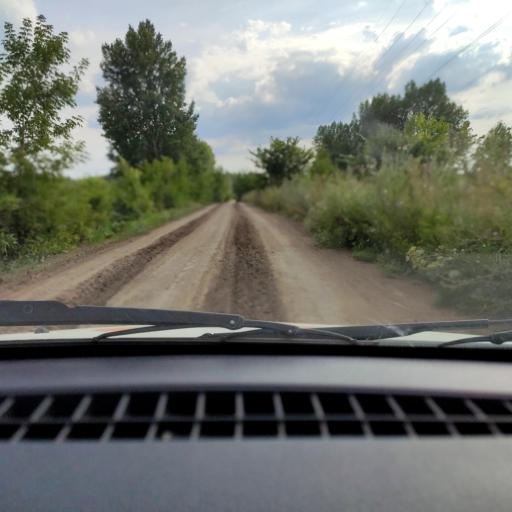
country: RU
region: Bashkortostan
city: Blagoveshchensk
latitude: 54.9214
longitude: 55.9365
